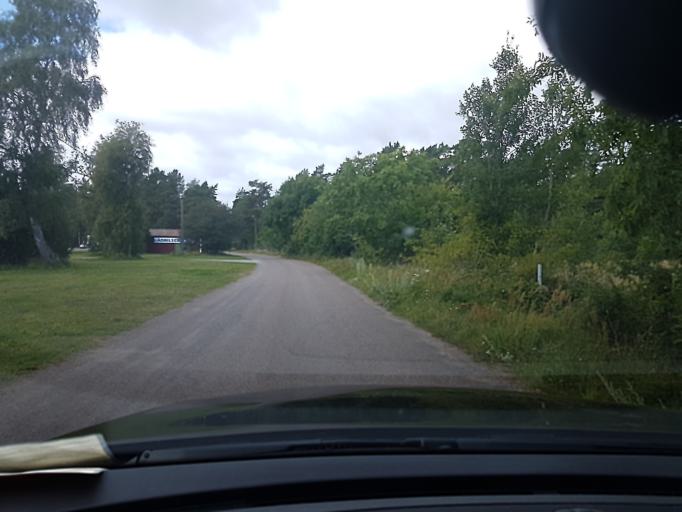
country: SE
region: Kalmar
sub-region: Borgholms Kommun
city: Borgholm
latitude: 57.1592
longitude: 17.0067
